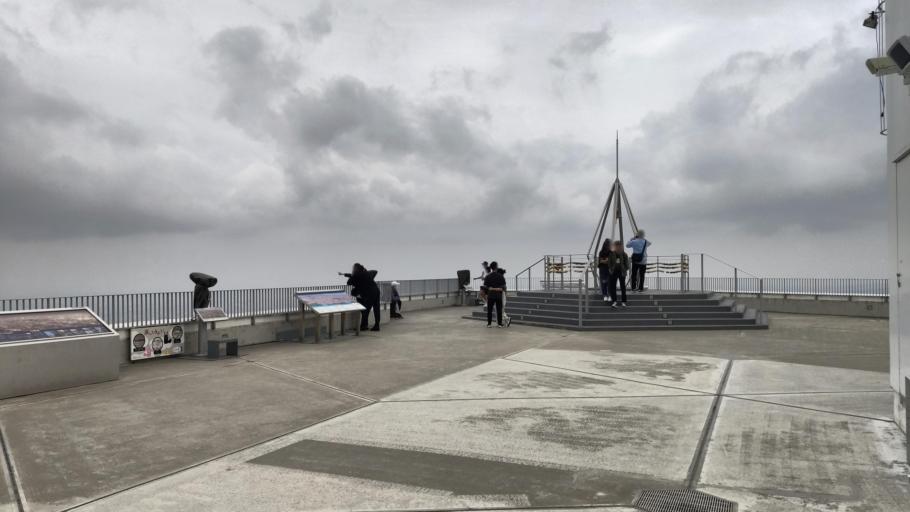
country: JP
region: Hokkaido
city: Sapporo
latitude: 43.0222
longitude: 141.3224
